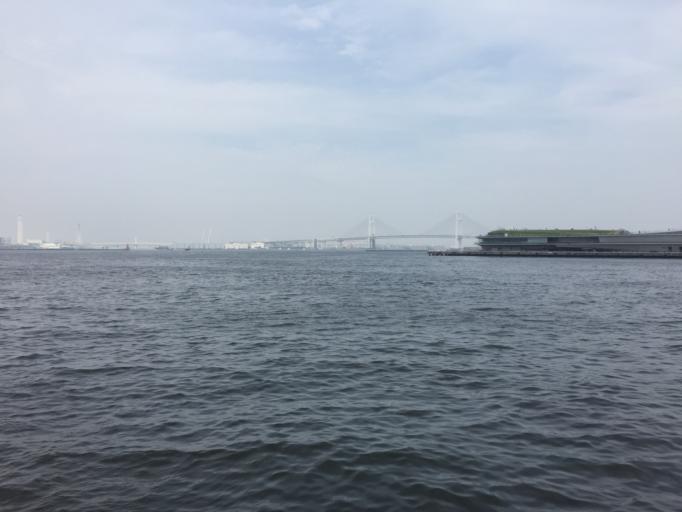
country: JP
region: Kanagawa
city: Yokohama
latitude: 35.4537
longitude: 139.6442
